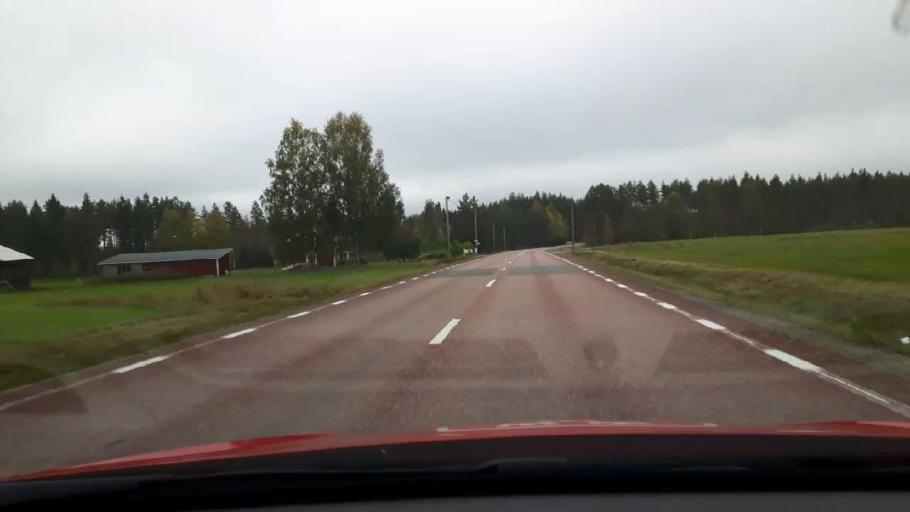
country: SE
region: Gaevleborg
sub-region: Ljusdals Kommun
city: Farila
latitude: 61.8403
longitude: 15.7509
